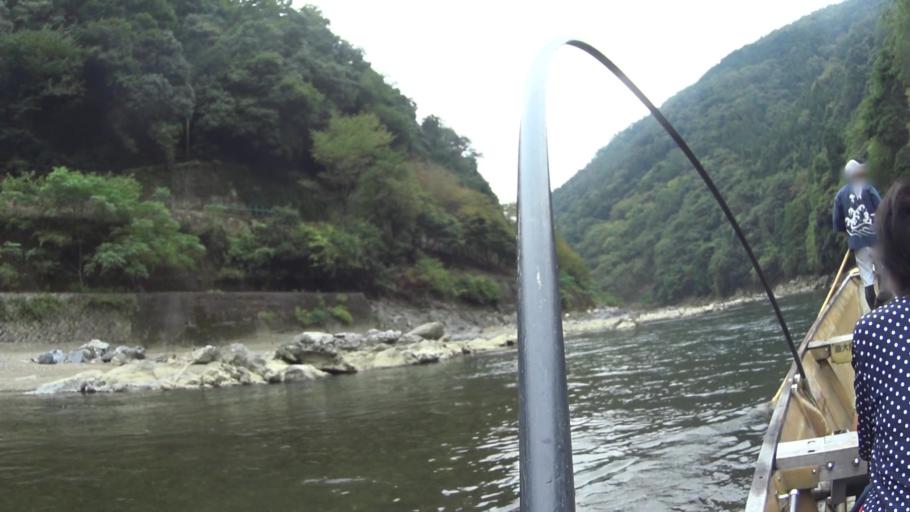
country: JP
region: Kyoto
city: Muko
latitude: 35.0190
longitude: 135.6579
